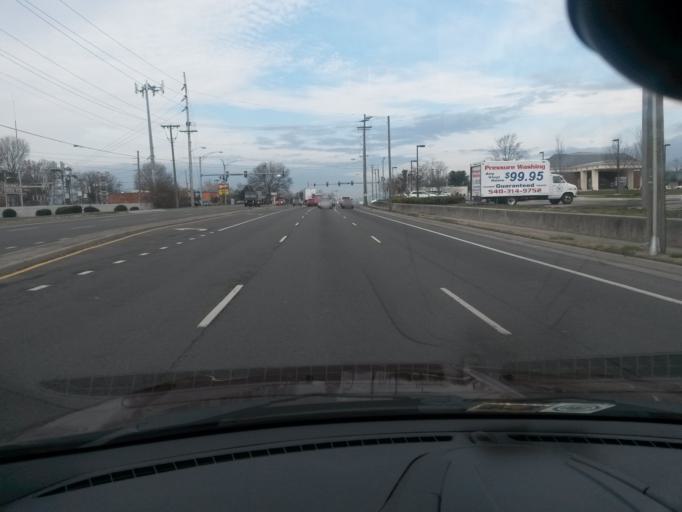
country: US
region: Virginia
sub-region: Roanoke County
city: Hollins
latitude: 37.3149
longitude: -79.9598
